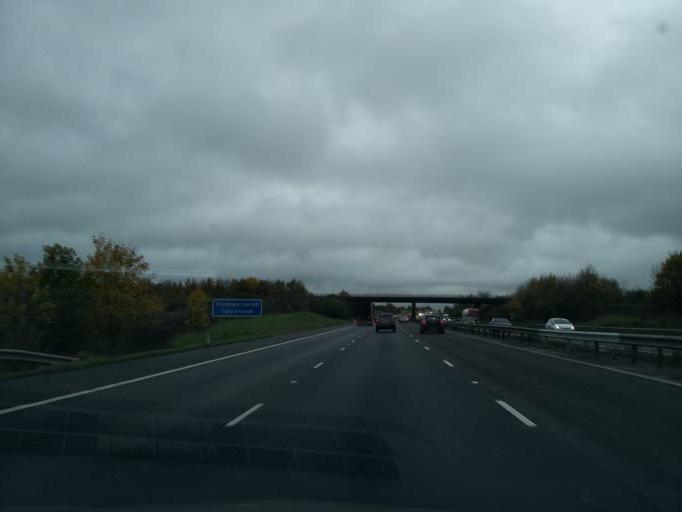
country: GB
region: England
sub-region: Oxfordshire
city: Bicester
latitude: 51.9039
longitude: -1.2061
